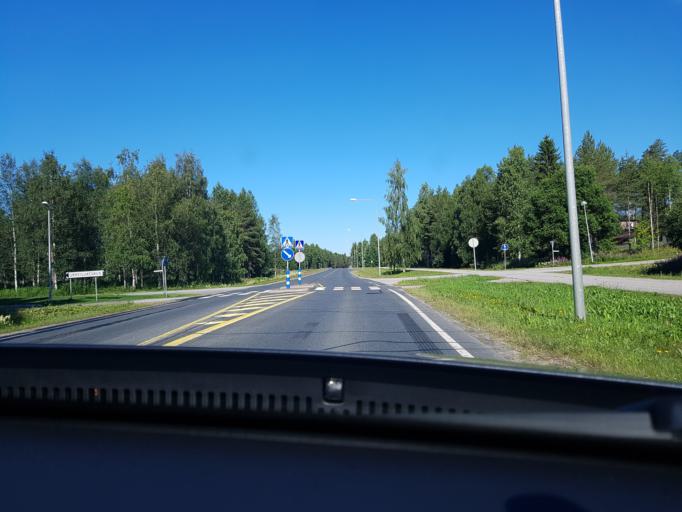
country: FI
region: Kainuu
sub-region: Kehys-Kainuu
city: Kuhmo
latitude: 64.1197
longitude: 29.5214
